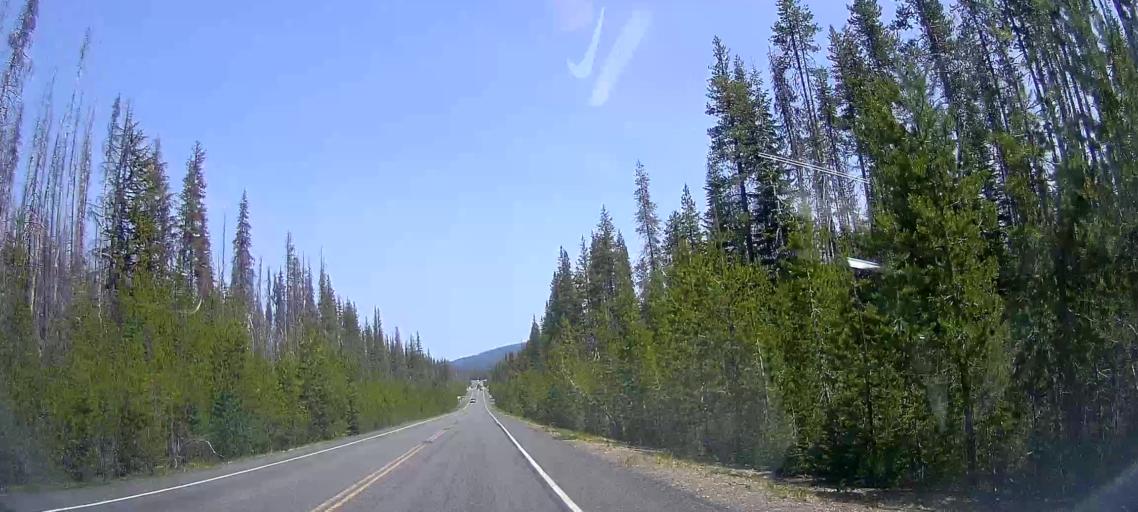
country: US
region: Oregon
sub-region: Lane County
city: Oakridge
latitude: 43.0730
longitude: -122.1187
